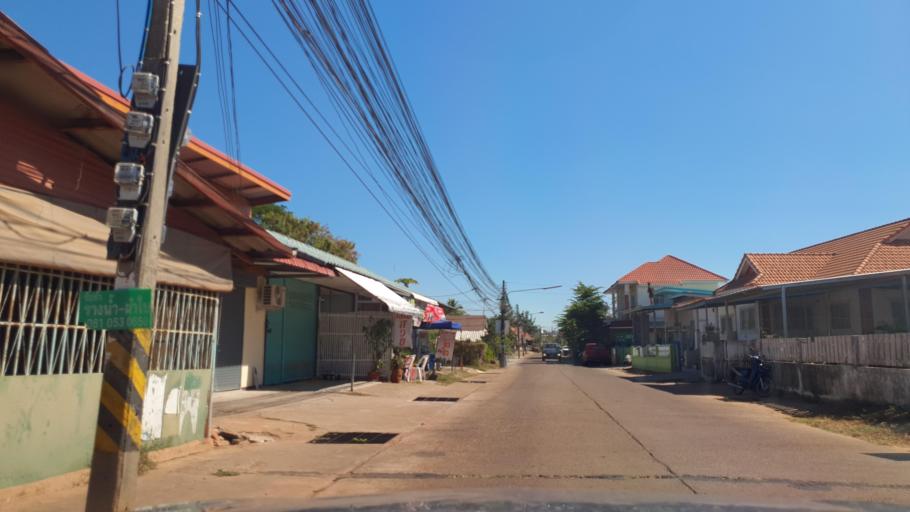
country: TH
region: Sakon Nakhon
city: Sakon Nakhon
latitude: 17.1571
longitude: 104.1231
